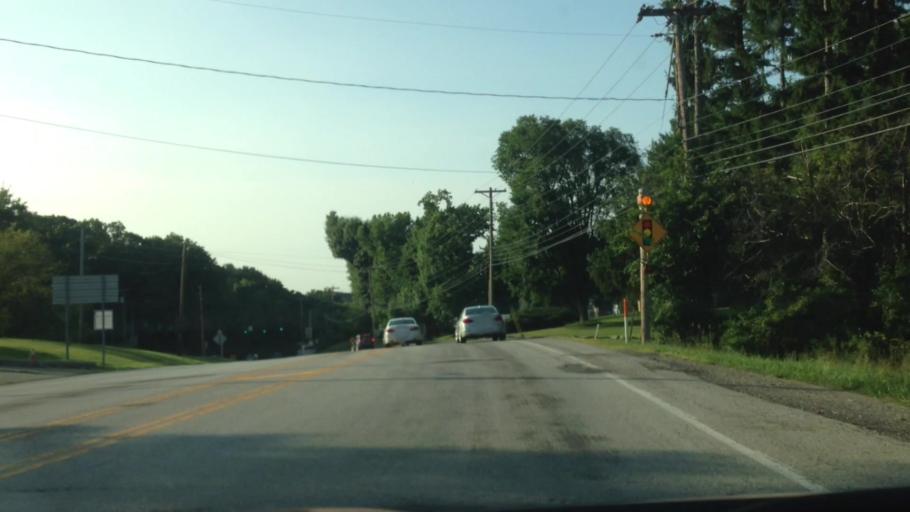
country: US
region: Ohio
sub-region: Summit County
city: Montrose-Ghent
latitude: 41.1528
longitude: -81.6332
